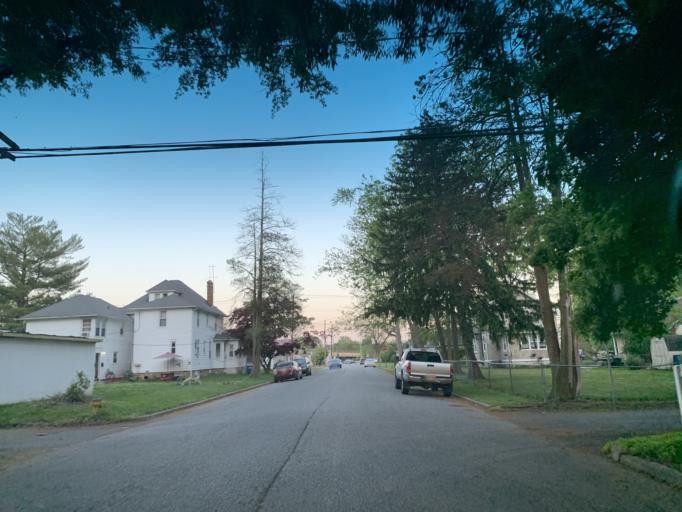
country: US
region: Maryland
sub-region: Harford County
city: Aberdeen
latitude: 39.5077
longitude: -76.1680
